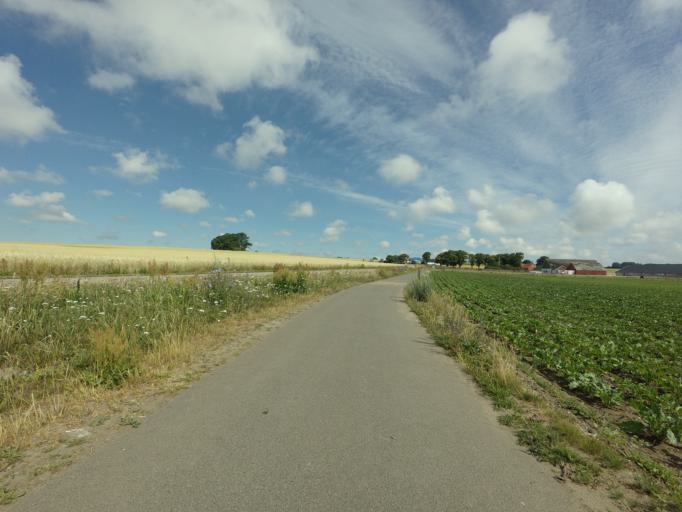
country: SE
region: Skane
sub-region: Simrishamns Kommun
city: Simrishamn
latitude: 55.4810
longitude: 14.2847
